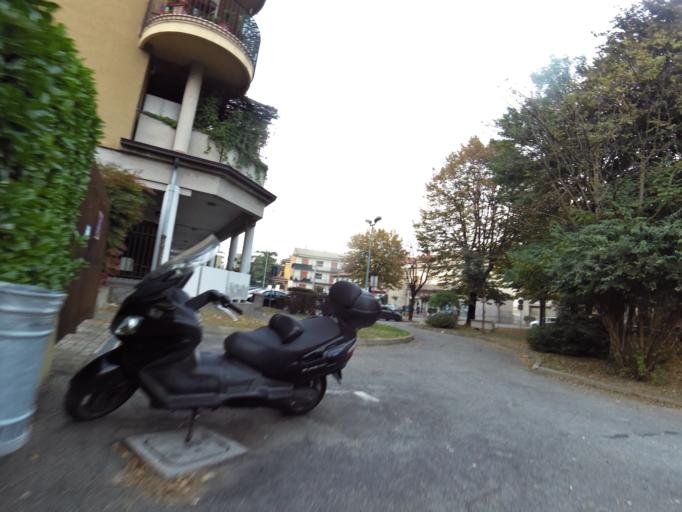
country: IT
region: Lombardy
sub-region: Citta metropolitana di Milano
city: Bettola-Zeloforomagno
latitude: 45.4258
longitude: 9.2972
